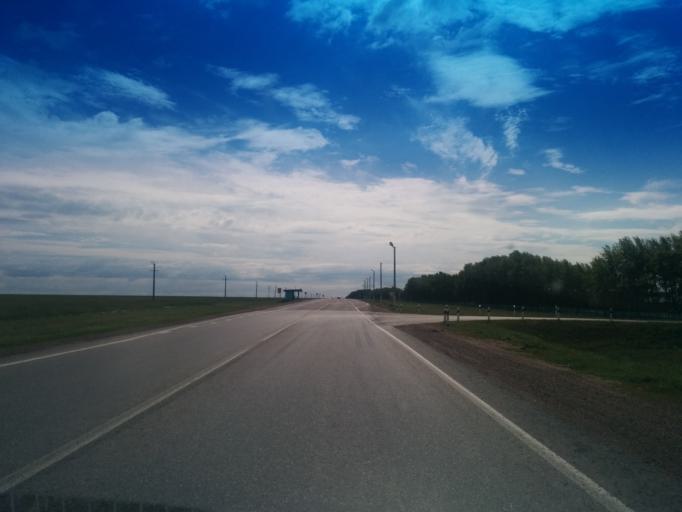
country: RU
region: Bashkortostan
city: Karmaskaly
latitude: 54.4264
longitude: 56.0307
